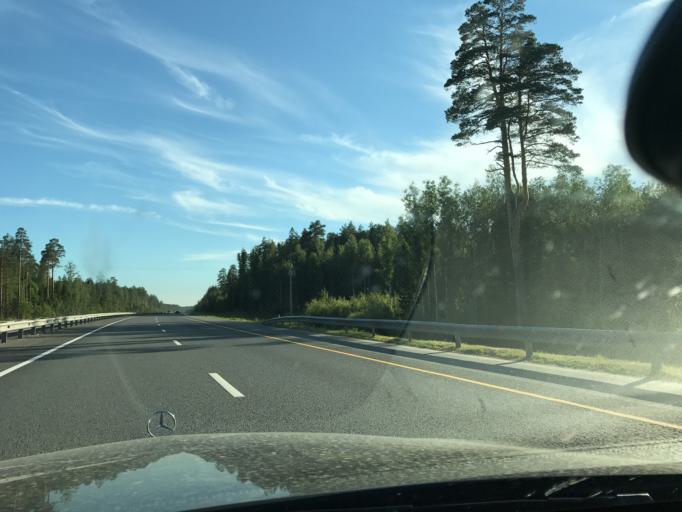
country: RU
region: Vladimir
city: Kameshkovo
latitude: 56.1748
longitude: 40.9440
